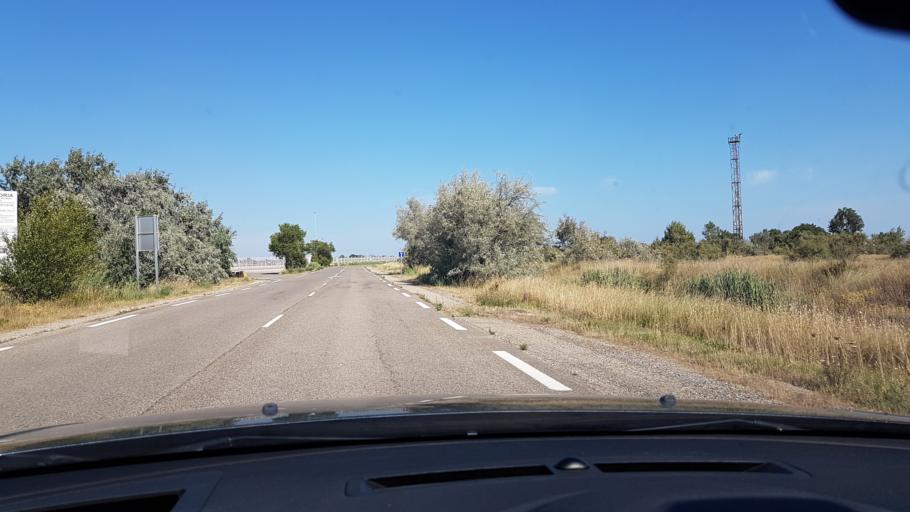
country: FR
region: Provence-Alpes-Cote d'Azur
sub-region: Departement des Bouches-du-Rhone
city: Port-Saint-Louis-du-Rhone
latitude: 43.3913
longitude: 4.8419
